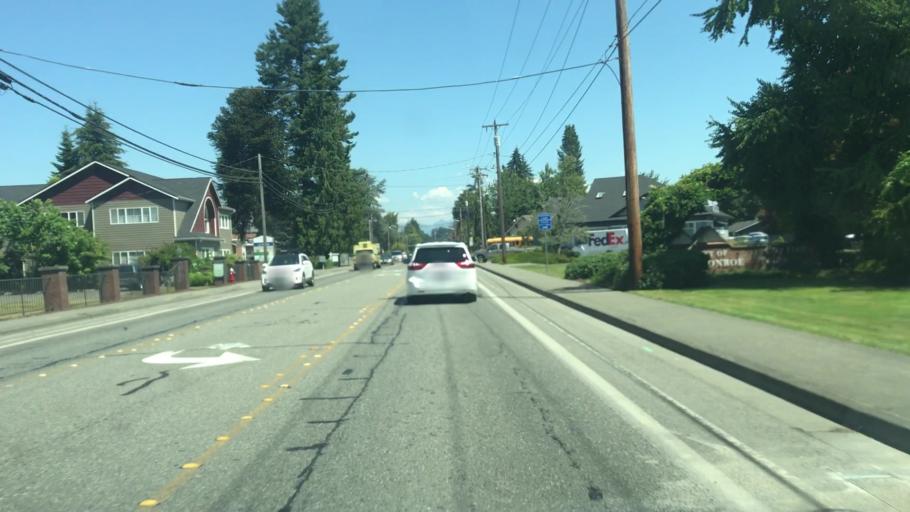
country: US
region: Washington
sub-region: Snohomish County
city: Monroe
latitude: 47.8521
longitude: -121.9822
